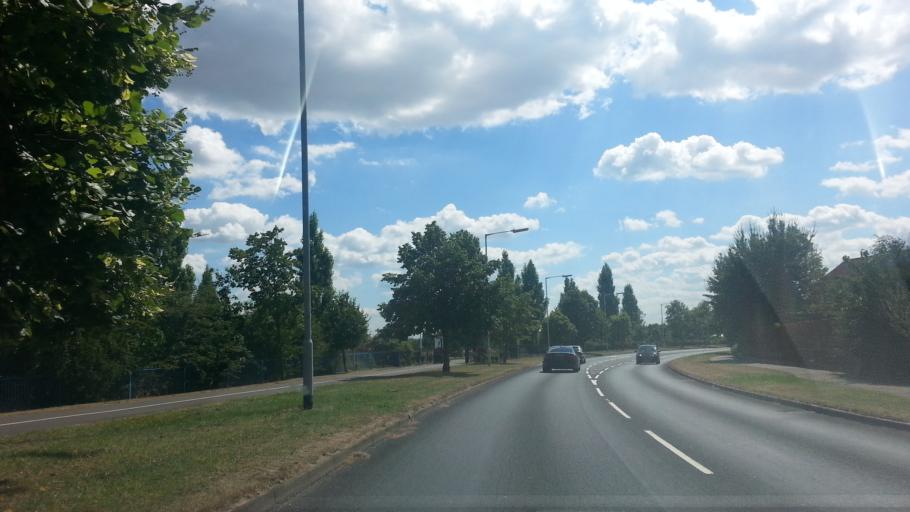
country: GB
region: England
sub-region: Essex
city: Chelmsford
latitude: 51.7371
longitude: 0.5115
